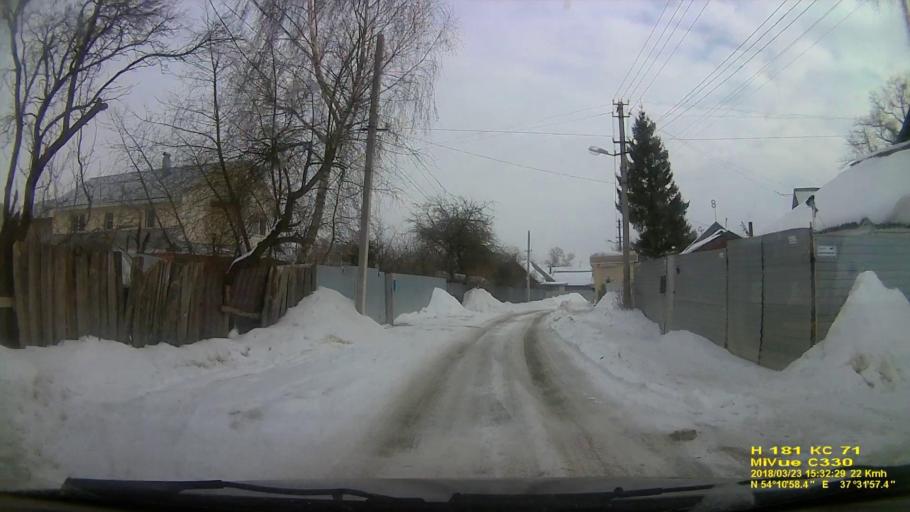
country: RU
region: Tula
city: Kosaya Gora
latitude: 54.1828
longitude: 37.5327
